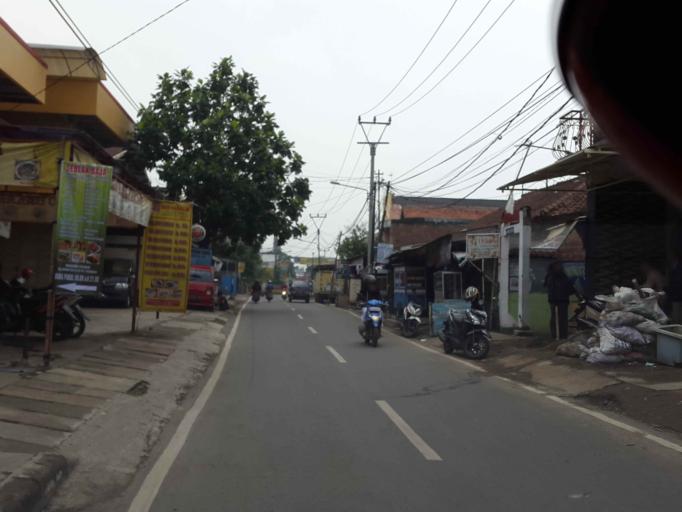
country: ID
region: West Java
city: Cimahi
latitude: -6.9183
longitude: 107.5637
